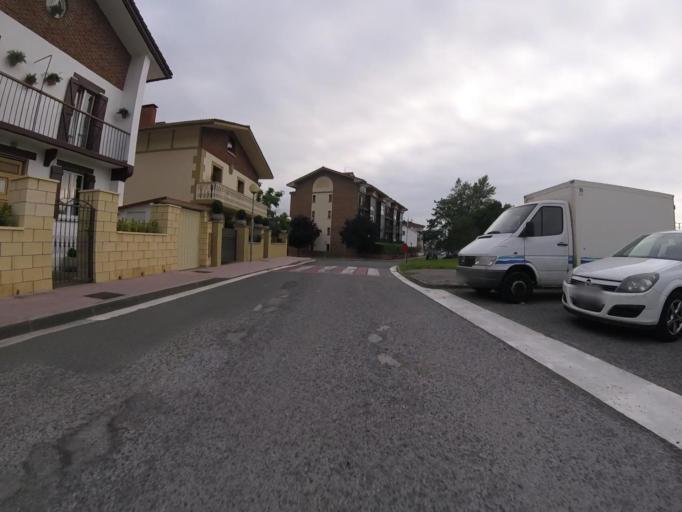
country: ES
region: Basque Country
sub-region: Provincia de Guipuzcoa
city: Lezo
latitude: 43.3083
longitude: -1.8779
